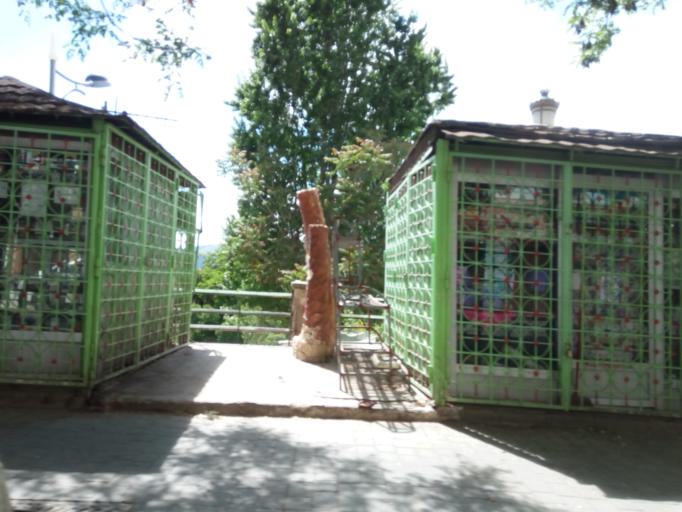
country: DZ
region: Constantine
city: Constantine
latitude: 36.3633
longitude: 6.6041
